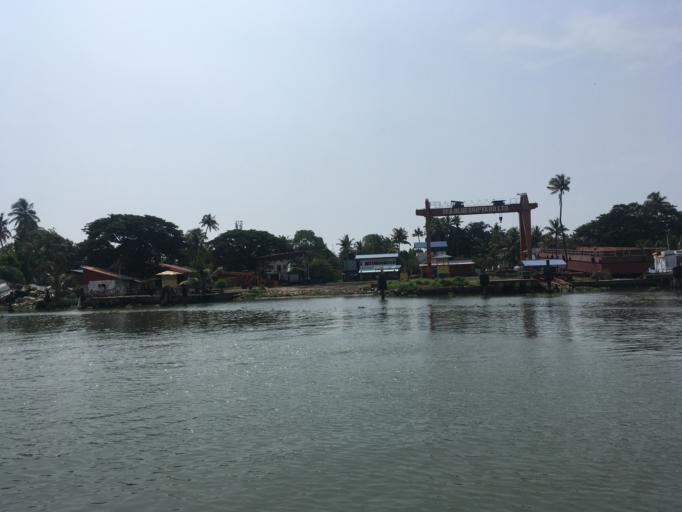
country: IN
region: Kerala
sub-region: Ernakulam
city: Cochin
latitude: 9.9761
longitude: 76.2444
